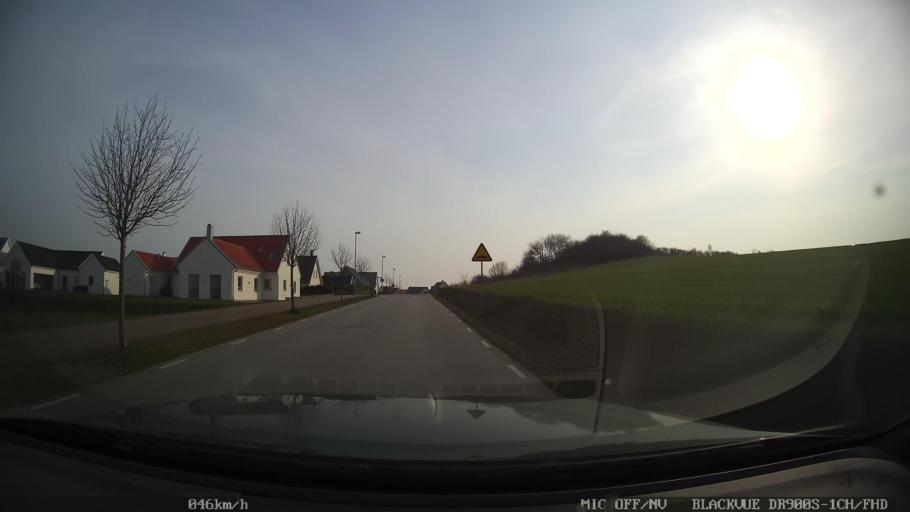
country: SE
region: Skane
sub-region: Ystads Kommun
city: Ystad
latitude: 55.4469
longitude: 13.7951
